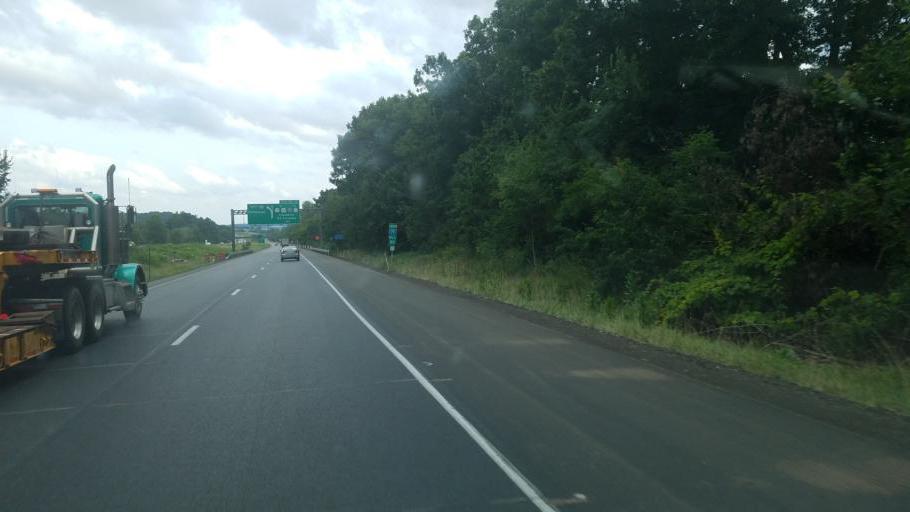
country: US
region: Pennsylvania
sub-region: Butler County
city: Fox Run
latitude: 40.7130
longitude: -80.1024
